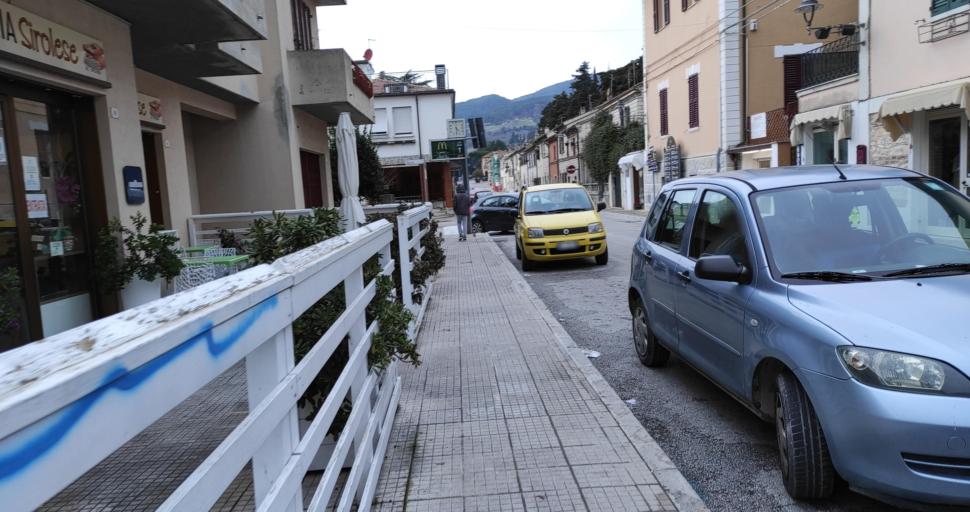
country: IT
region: The Marches
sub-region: Provincia di Ancona
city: Sirolo
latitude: 43.5250
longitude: 13.6177
